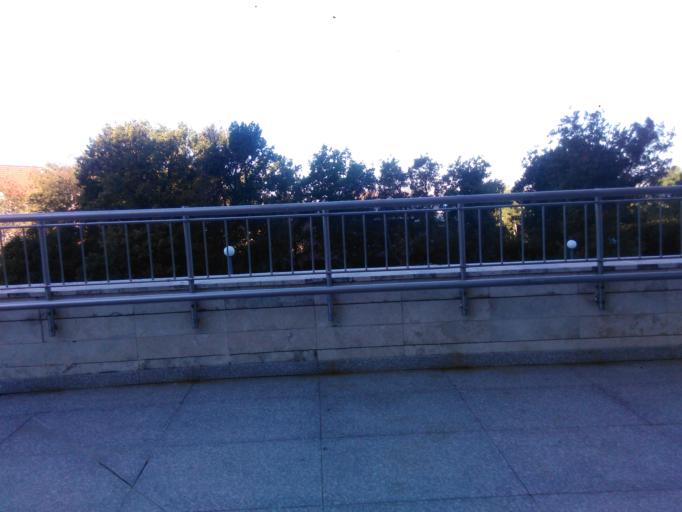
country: RU
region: Krasnodarskiy
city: Gelendzhik
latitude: 44.5517
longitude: 38.0537
